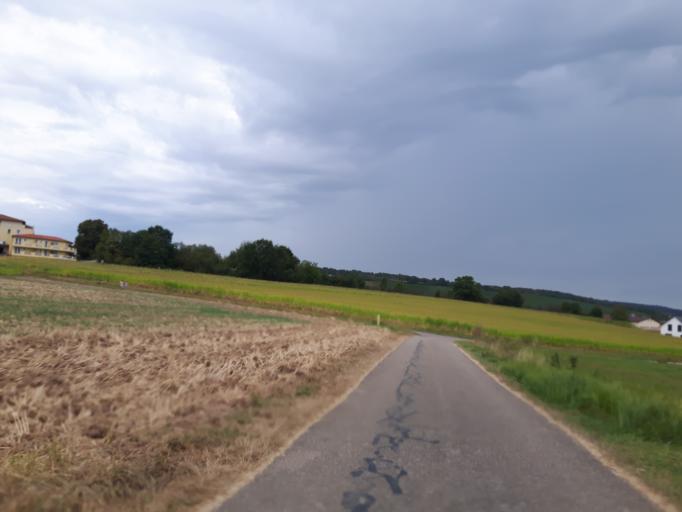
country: DE
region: Baden-Wuerttemberg
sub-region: Regierungsbezirk Stuttgart
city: Zaberfeld
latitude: 49.0548
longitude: 8.9185
